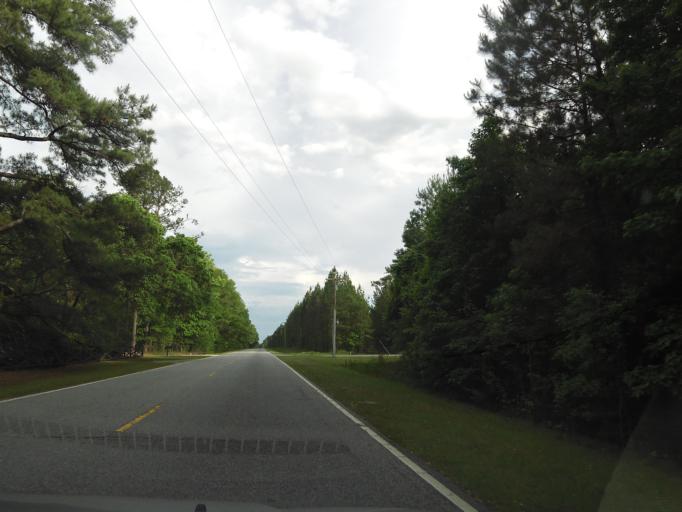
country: US
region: South Carolina
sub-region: Hampton County
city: Estill
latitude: 32.5698
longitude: -81.1833
